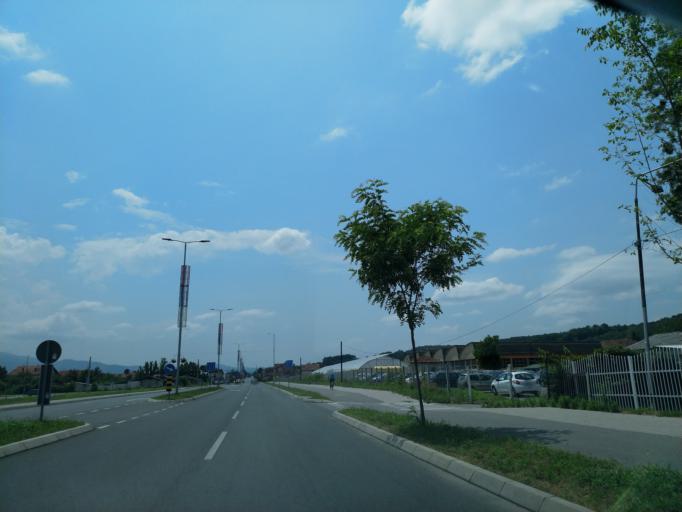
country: RS
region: Central Serbia
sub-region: Rasinski Okrug
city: Krusevac
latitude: 43.5580
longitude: 21.3326
